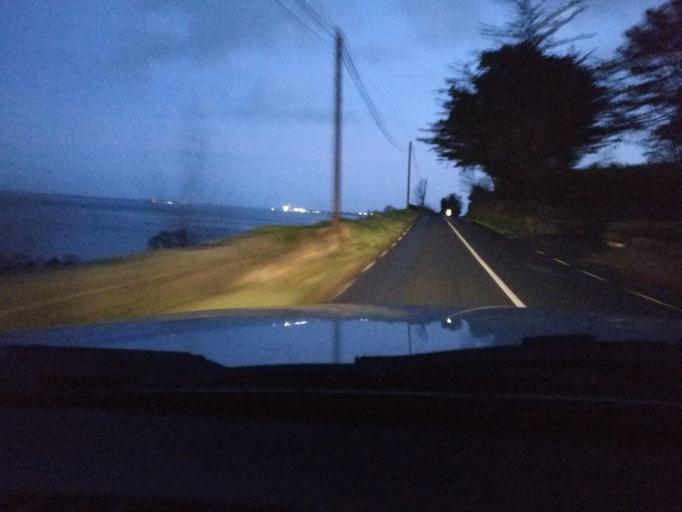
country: IE
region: Leinster
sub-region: Lu
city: Carlingford
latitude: 54.0567
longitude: -6.1990
